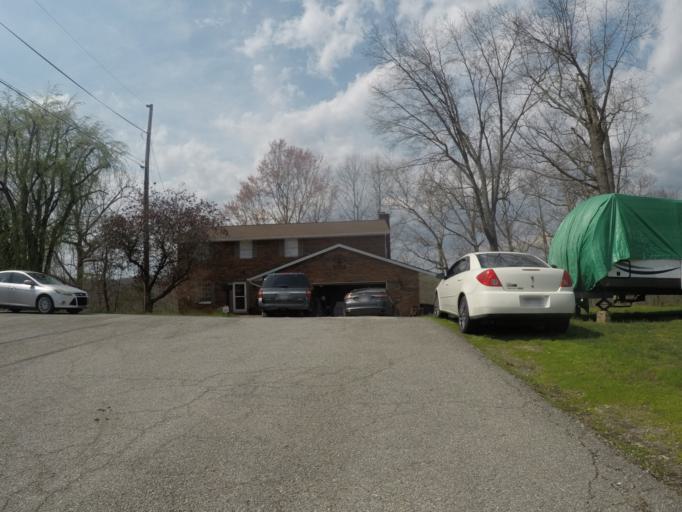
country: US
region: West Virginia
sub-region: Cabell County
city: Pea Ridge
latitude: 38.3996
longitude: -82.3342
